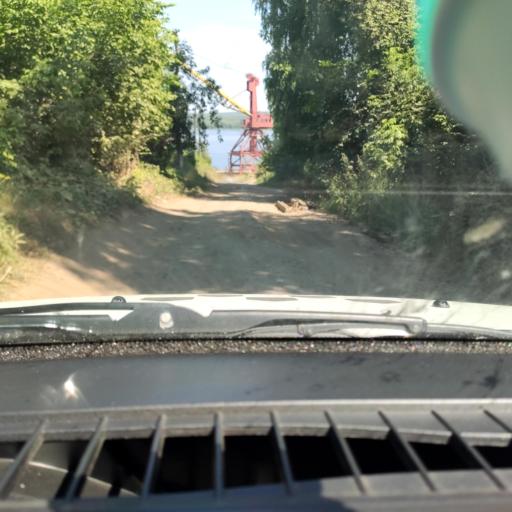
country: RU
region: Perm
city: Okhansk
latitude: 57.7245
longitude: 55.3972
